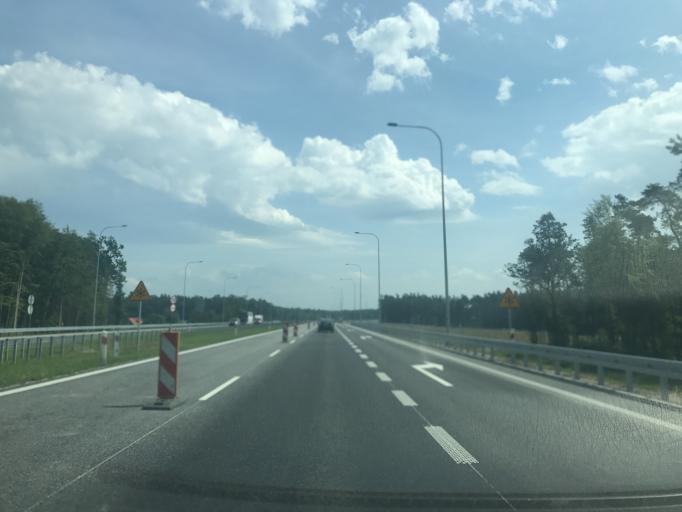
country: PL
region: Warmian-Masurian Voivodeship
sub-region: Powiat ostrodzki
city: Ostroda
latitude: 53.7305
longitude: 19.9315
